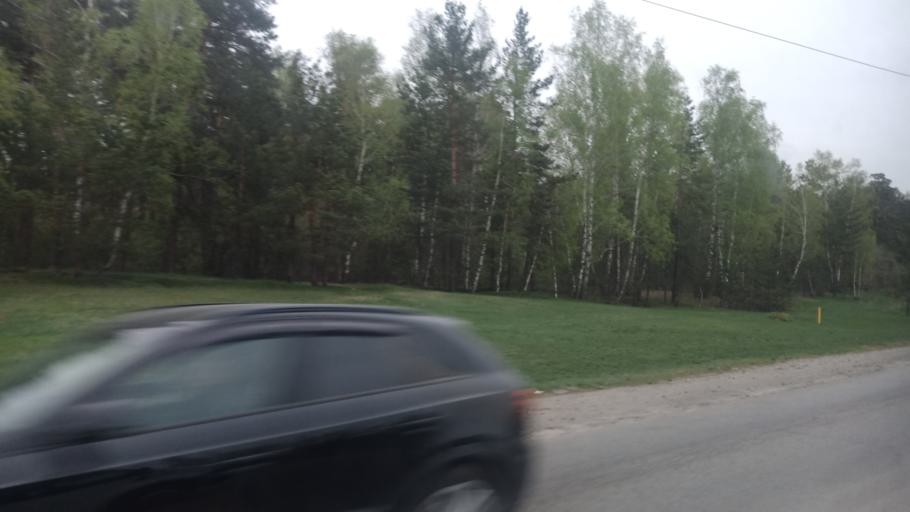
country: RU
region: Altai Krai
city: Yuzhnyy
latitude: 53.2610
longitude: 83.7011
